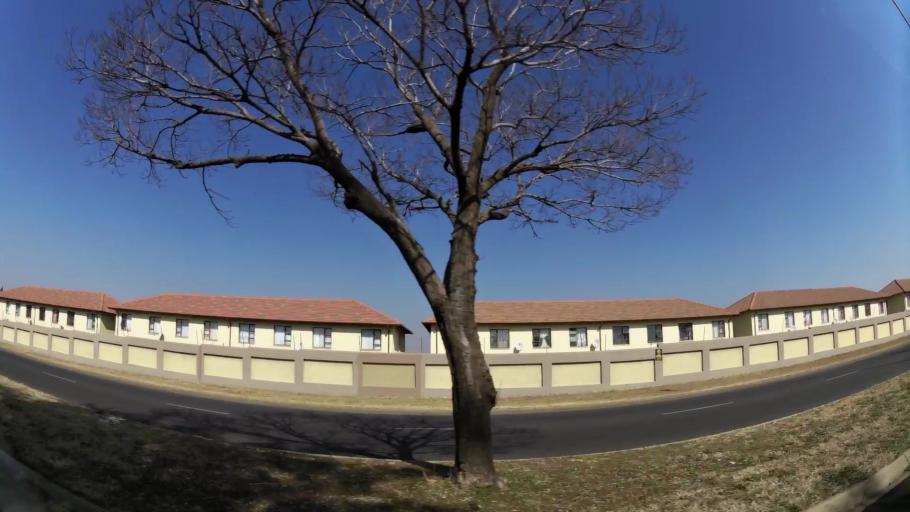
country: ZA
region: Gauteng
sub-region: Ekurhuleni Metropolitan Municipality
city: Boksburg
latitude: -26.2384
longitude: 28.2869
